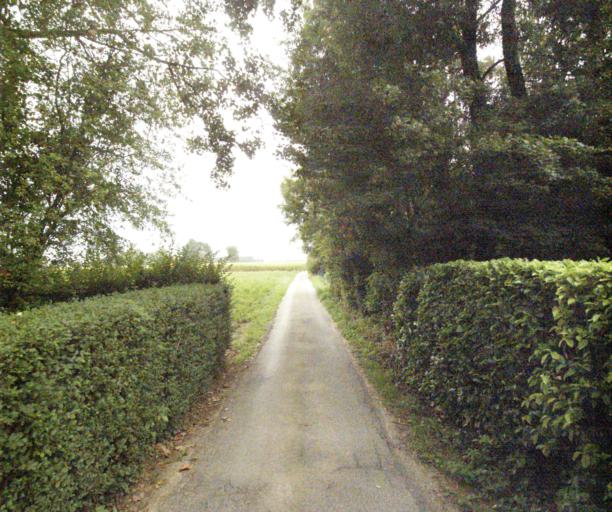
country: FR
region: Nord-Pas-de-Calais
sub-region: Departement du Nord
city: Sailly-lez-Lannoy
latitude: 50.6429
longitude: 3.2181
